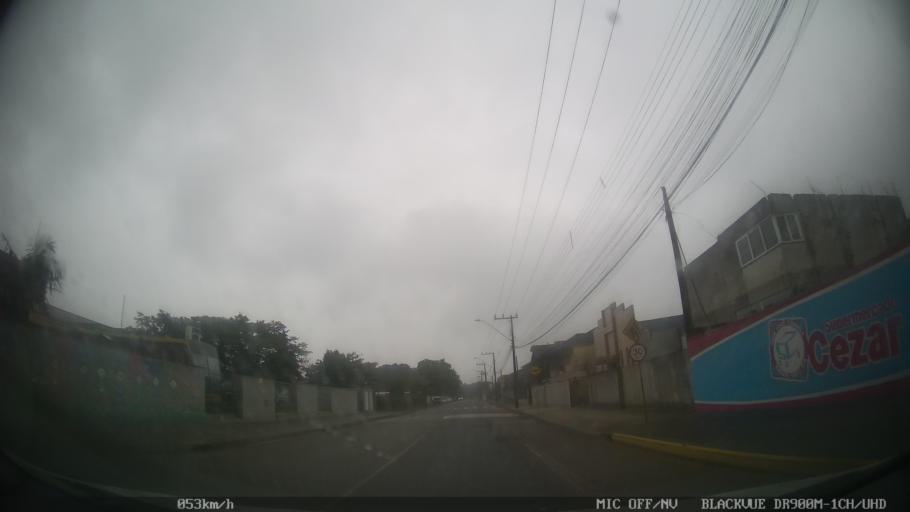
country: BR
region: Santa Catarina
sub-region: Joinville
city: Joinville
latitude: -26.2067
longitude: -48.8294
